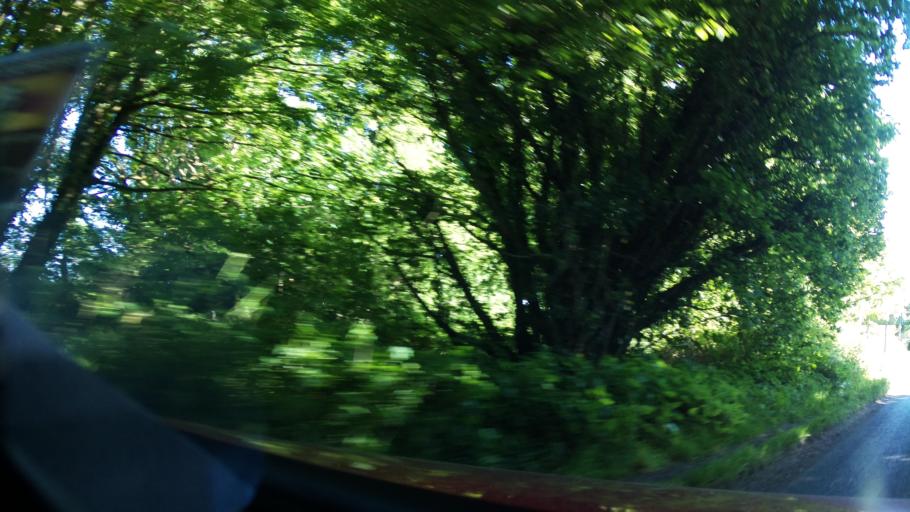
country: GB
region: England
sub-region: Dorset
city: Lyme Regis
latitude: 50.7682
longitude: -2.9538
